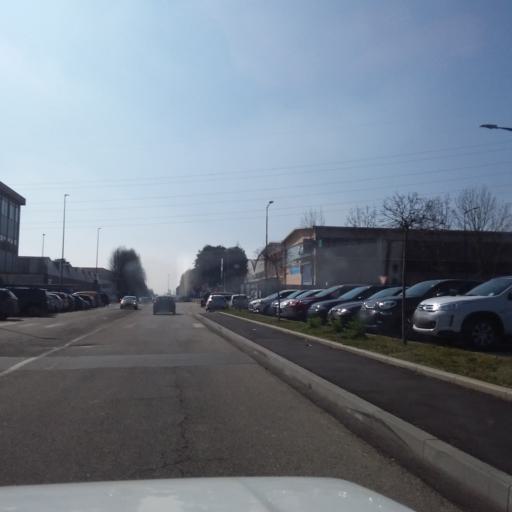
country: IT
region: Piedmont
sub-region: Provincia di Torino
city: Tetti Neirotti
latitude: 45.0674
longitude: 7.5514
